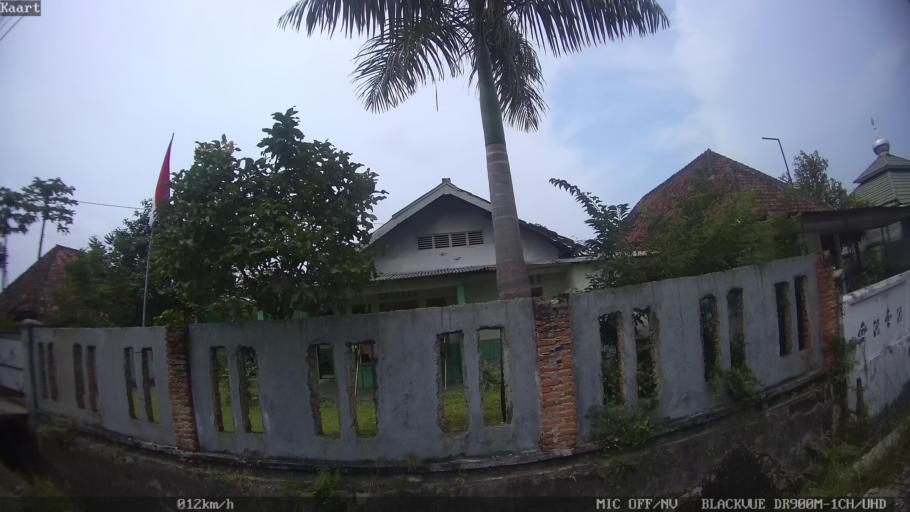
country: ID
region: Lampung
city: Bandarlampung
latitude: -5.4171
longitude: 105.2628
